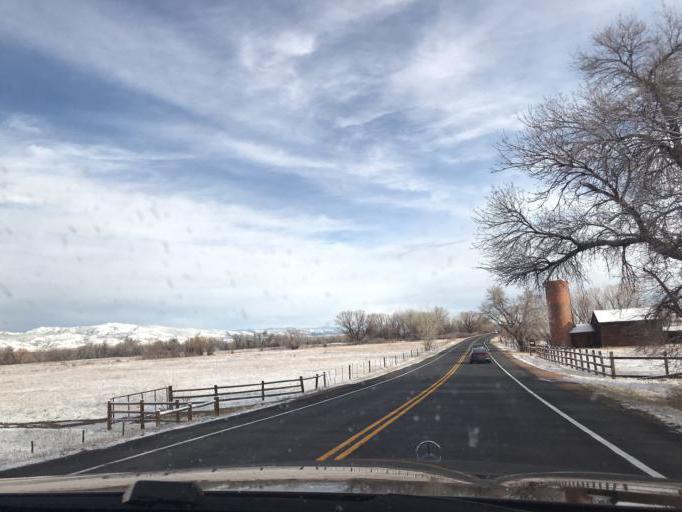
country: US
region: Colorado
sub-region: Boulder County
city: Superior
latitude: 39.9879
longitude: -105.2128
